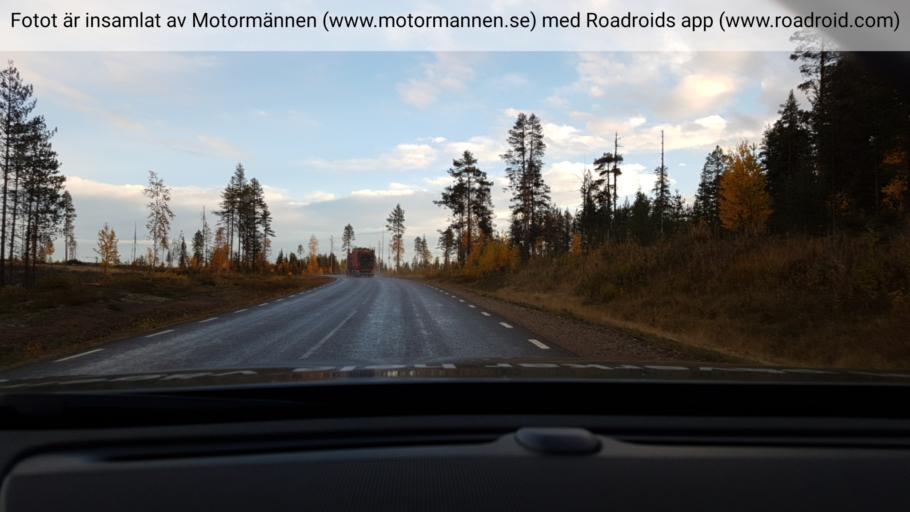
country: SE
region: Norrbotten
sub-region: Overkalix Kommun
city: OEverkalix
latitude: 66.6533
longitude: 22.6909
